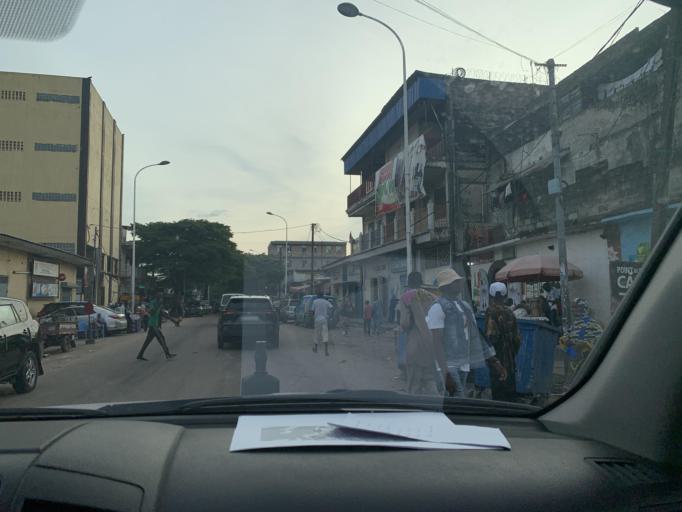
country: CG
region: Brazzaville
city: Brazzaville
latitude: -4.2652
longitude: 15.2867
